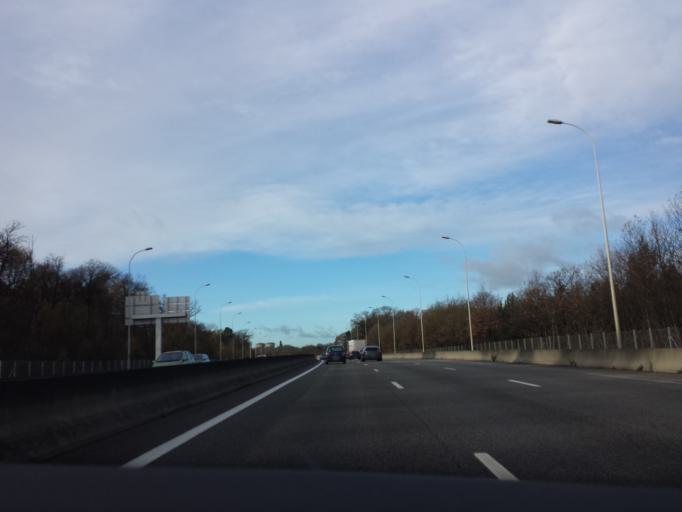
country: FR
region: Ile-de-France
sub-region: Departement des Yvelines
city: Versailles
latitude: 48.7881
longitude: 2.1420
